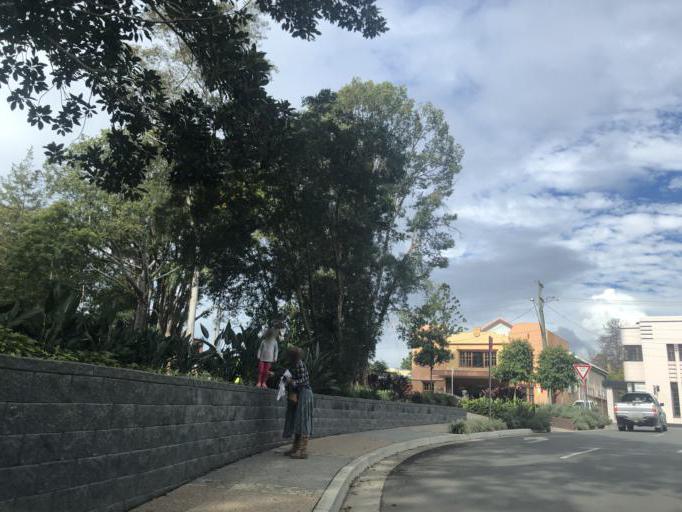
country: AU
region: New South Wales
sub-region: Bellingen
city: Bellingen
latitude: -30.4519
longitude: 152.8982
